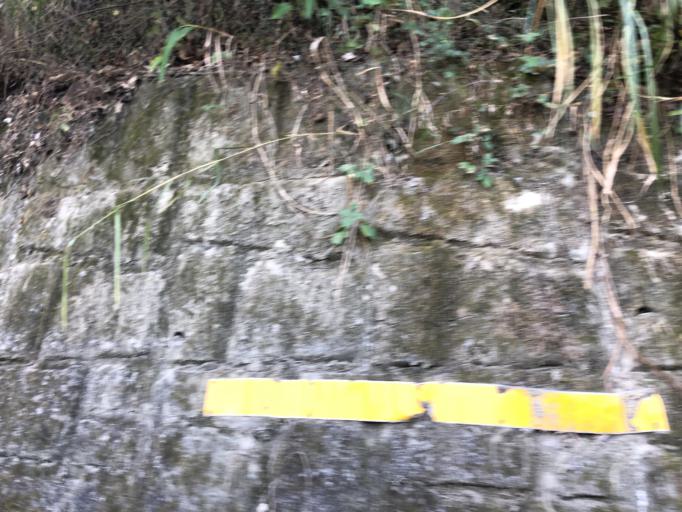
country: TW
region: Taiwan
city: Yujing
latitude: 23.0174
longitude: 120.3829
